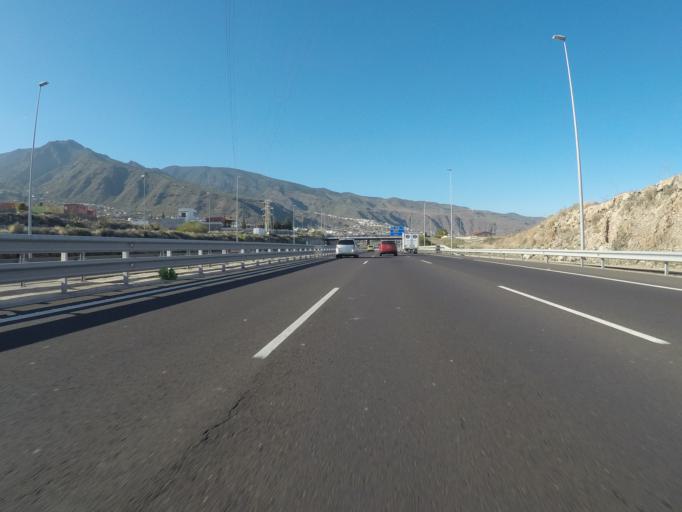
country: ES
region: Canary Islands
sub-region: Provincia de Santa Cruz de Tenerife
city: Candelaria
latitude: 28.3489
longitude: -16.3734
